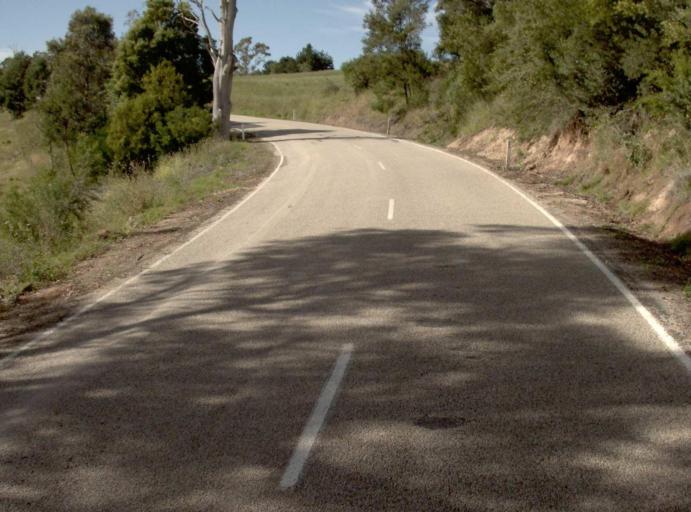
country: AU
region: Victoria
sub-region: East Gippsland
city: Lakes Entrance
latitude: -37.5130
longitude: 148.1675
